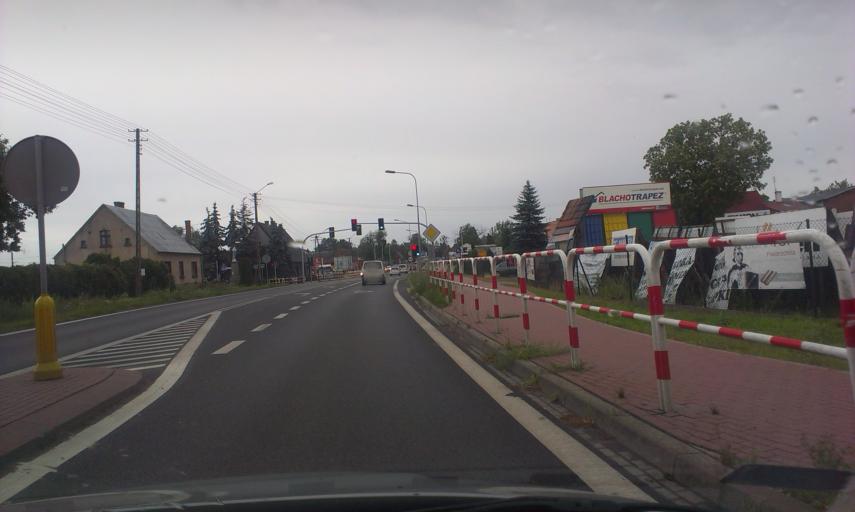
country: PL
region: Greater Poland Voivodeship
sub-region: Powiat obornicki
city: Oborniki
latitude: 52.6259
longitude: 16.8089
